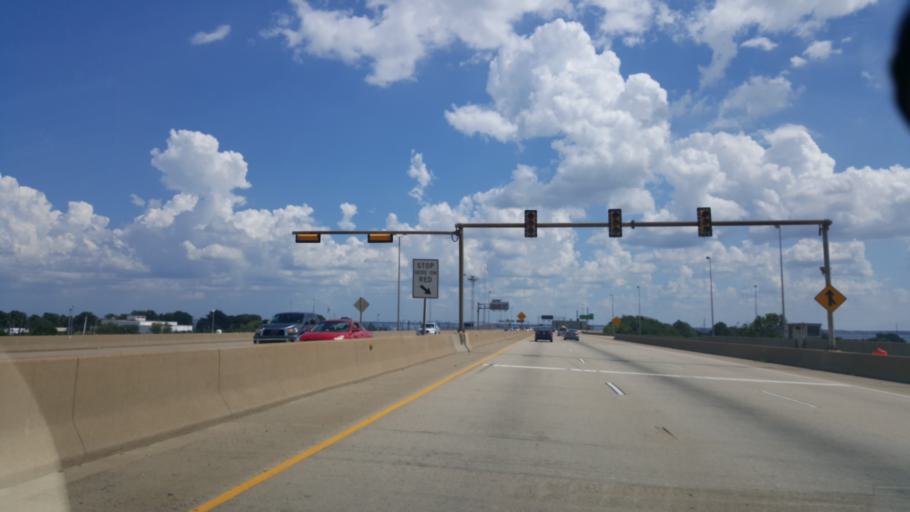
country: US
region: Virginia
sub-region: City of Newport News
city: Newport News
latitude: 36.9720
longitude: -76.4187
